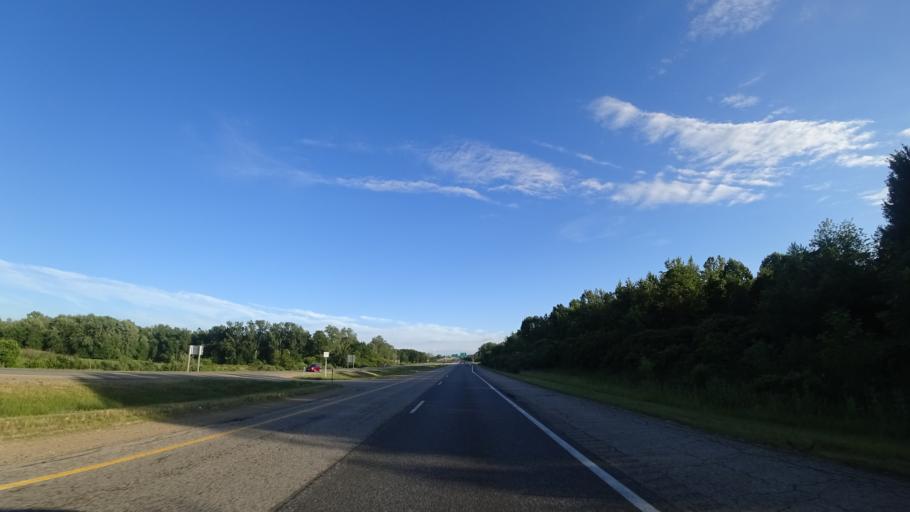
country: US
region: Michigan
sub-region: Berrien County
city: Benton Heights
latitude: 42.1433
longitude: -86.3685
